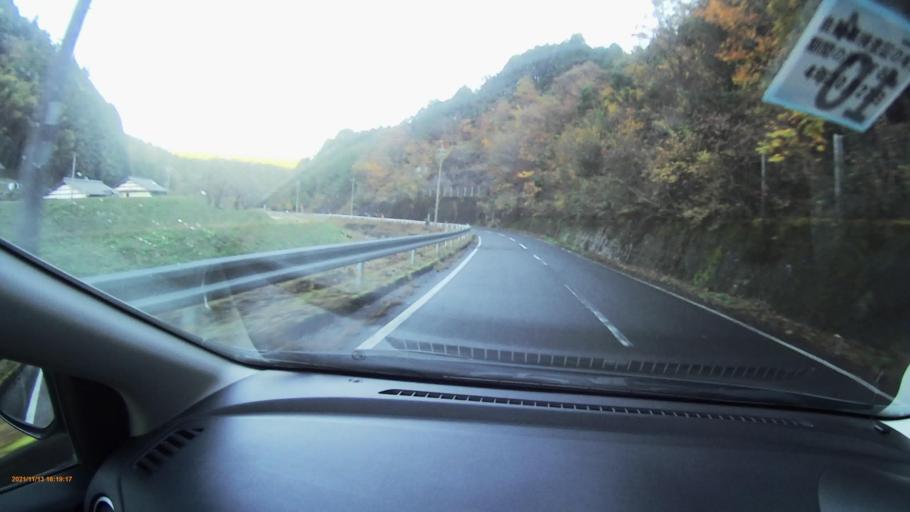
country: JP
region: Gifu
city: Nakatsugawa
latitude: 35.5692
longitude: 137.5069
